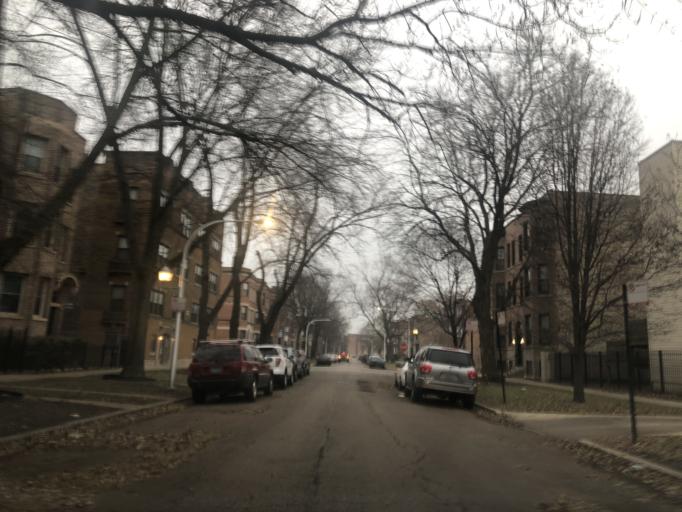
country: US
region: Illinois
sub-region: Cook County
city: Chicago
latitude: 41.7830
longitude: -87.5995
